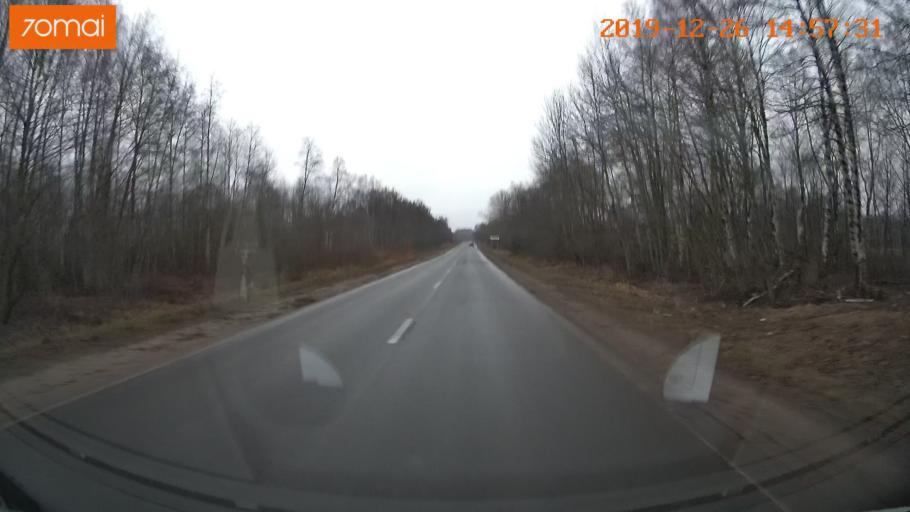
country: RU
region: Jaroslavl
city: Rybinsk
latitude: 58.2818
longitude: 38.8622
